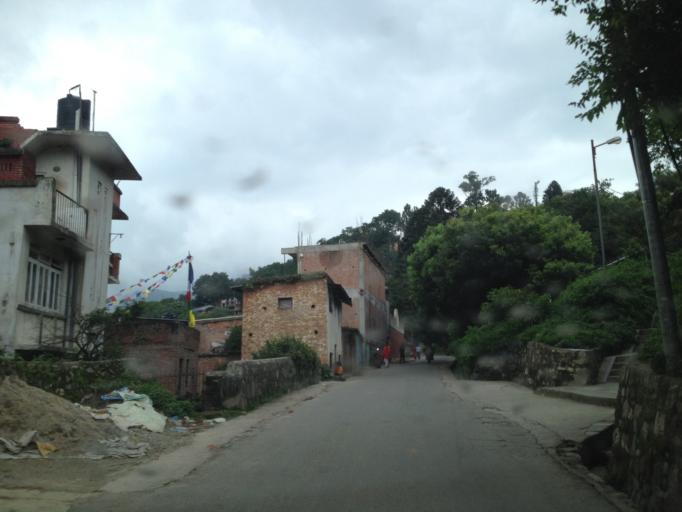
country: NP
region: Central Region
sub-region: Bagmati Zone
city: Kathmandu
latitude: 27.7136
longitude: 85.2893
